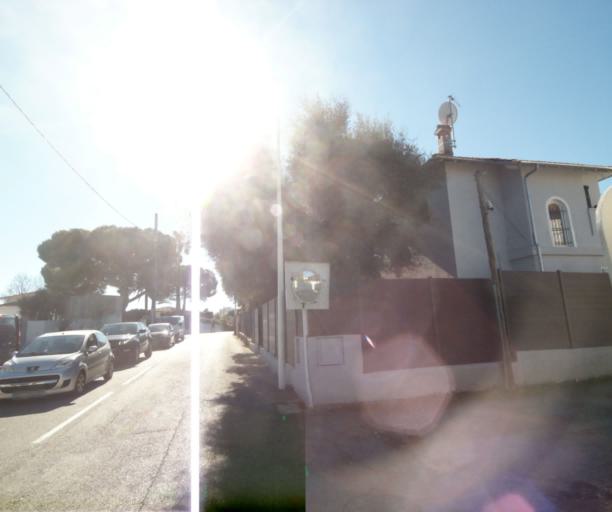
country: FR
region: Provence-Alpes-Cote d'Azur
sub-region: Departement des Alpes-Maritimes
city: Antibes
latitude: 43.5563
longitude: 7.1286
